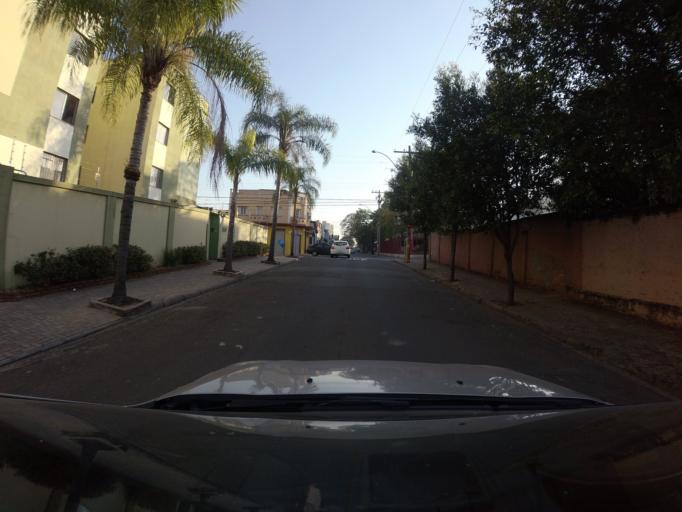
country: BR
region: Sao Paulo
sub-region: Piracicaba
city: Piracicaba
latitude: -22.7317
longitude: -47.6449
